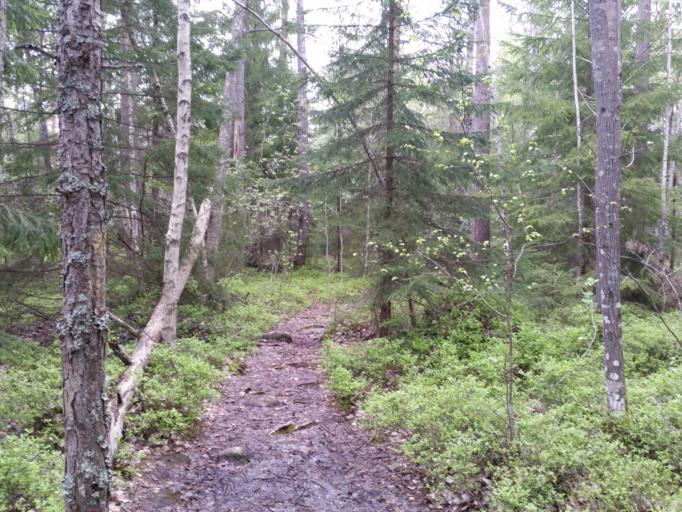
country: SE
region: Stockholm
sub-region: Sollentuna Kommun
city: Sollentuna
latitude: 59.4686
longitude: 17.9497
